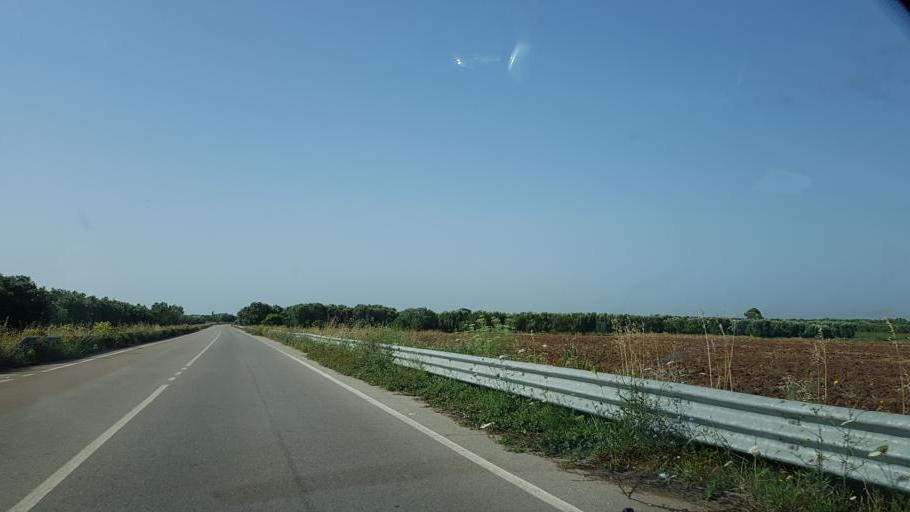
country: IT
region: Apulia
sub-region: Provincia di Brindisi
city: San Pancrazio Salentino
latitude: 40.4782
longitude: 17.8365
